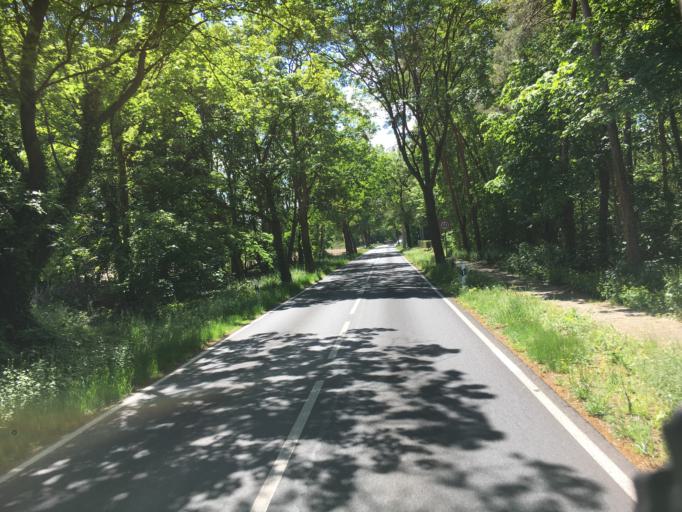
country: DE
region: Brandenburg
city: Am Mellensee
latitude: 52.2459
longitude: 13.3402
